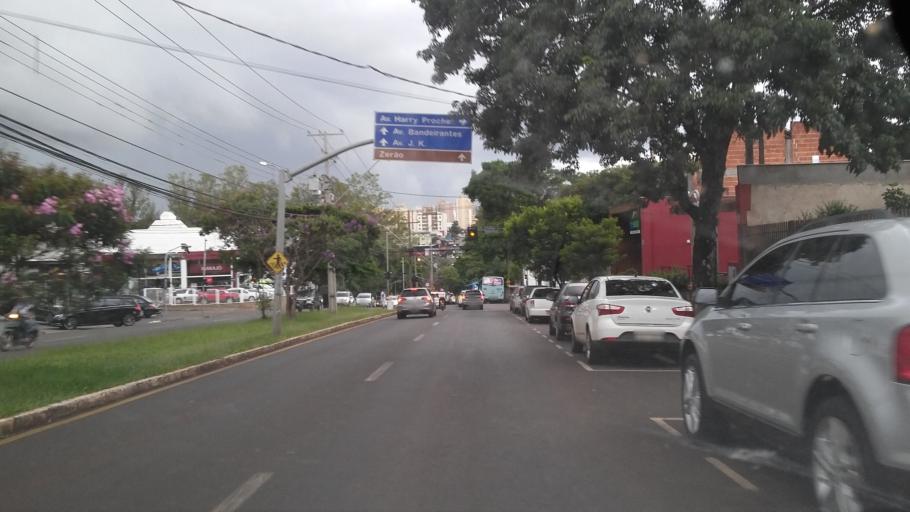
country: BR
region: Parana
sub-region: Londrina
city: Londrina
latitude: -23.3325
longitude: -51.1676
